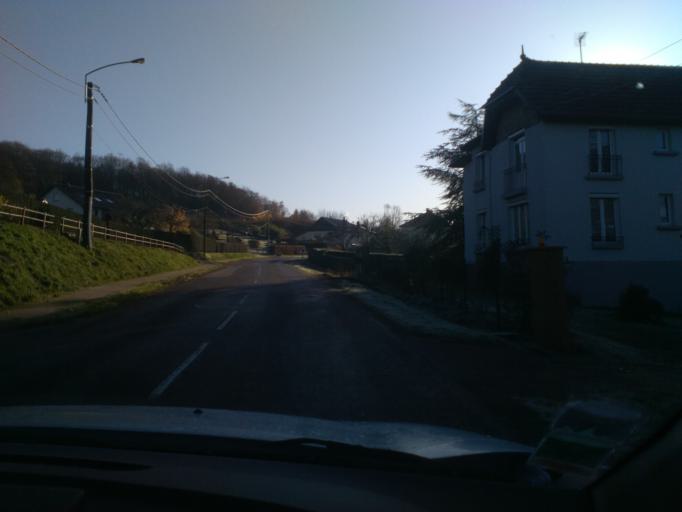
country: FR
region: Lorraine
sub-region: Departement des Vosges
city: Xertigny
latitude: 48.0528
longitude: 6.3743
